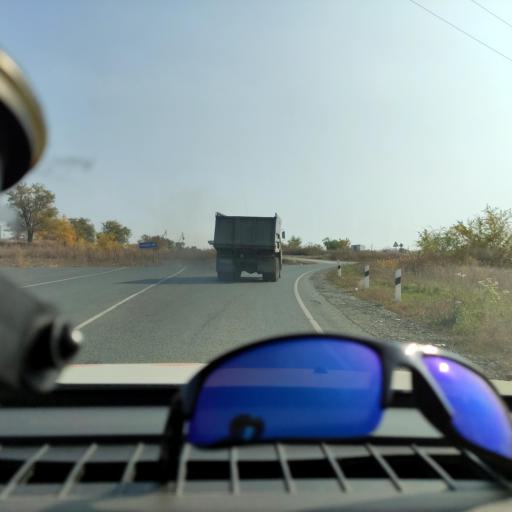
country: RU
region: Samara
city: Chapayevsk
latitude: 52.9996
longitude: 49.7671
